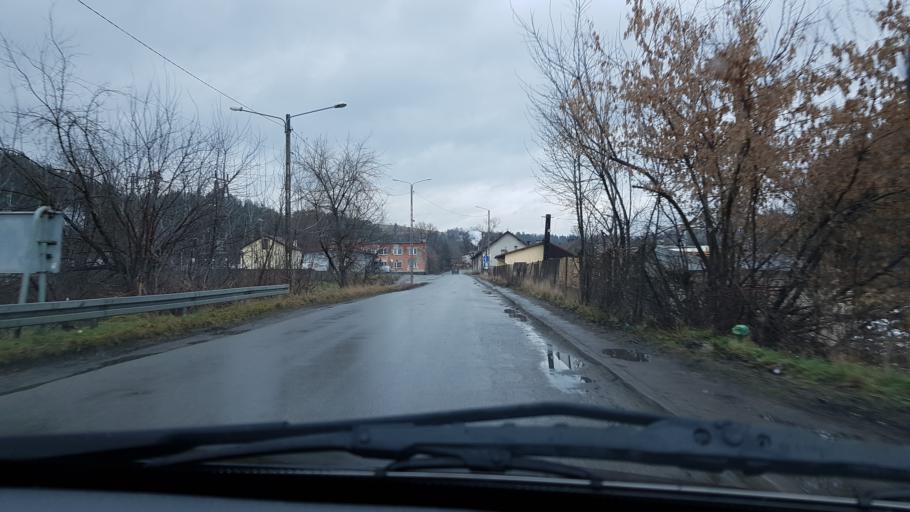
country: PL
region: Lesser Poland Voivodeship
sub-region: Powiat suski
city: Jordanow
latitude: 49.6362
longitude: 19.8310
